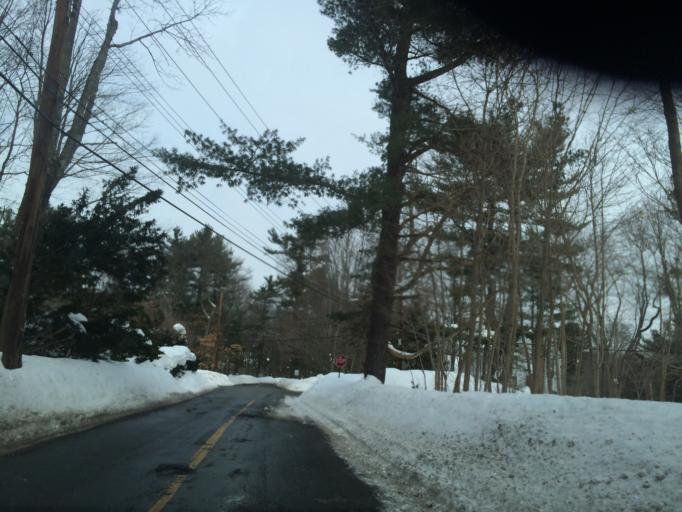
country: US
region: Massachusetts
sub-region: Middlesex County
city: Weston
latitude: 42.3367
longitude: -71.3144
